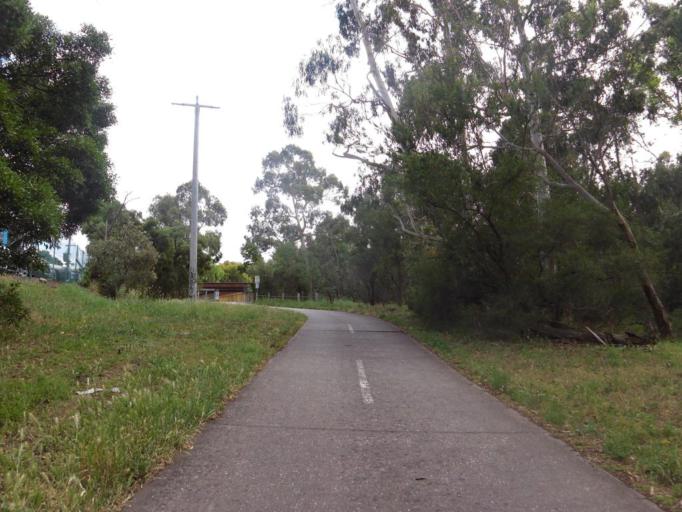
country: AU
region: Victoria
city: Alphington
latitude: -37.7675
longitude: 145.0314
